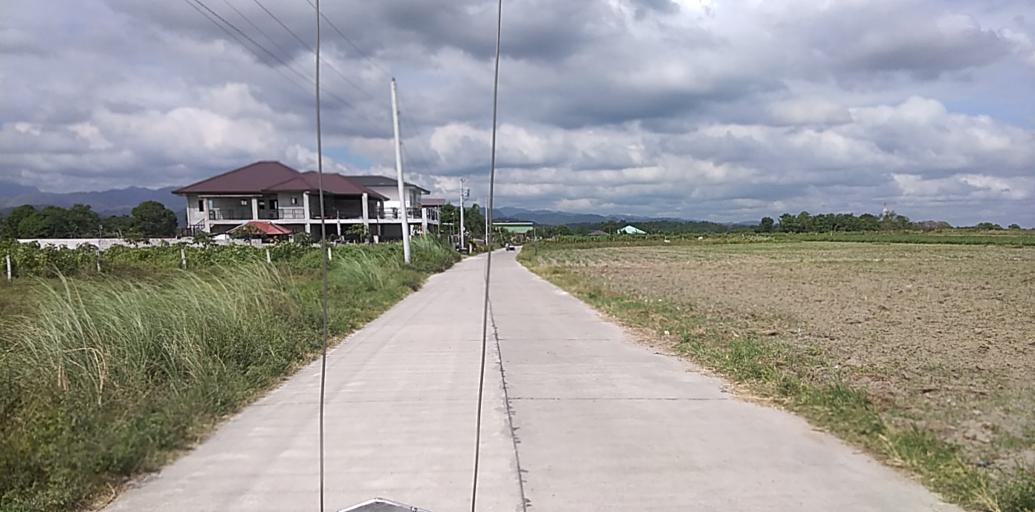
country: PH
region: Central Luzon
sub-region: Province of Pampanga
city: Porac
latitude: 15.0598
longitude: 120.5386
